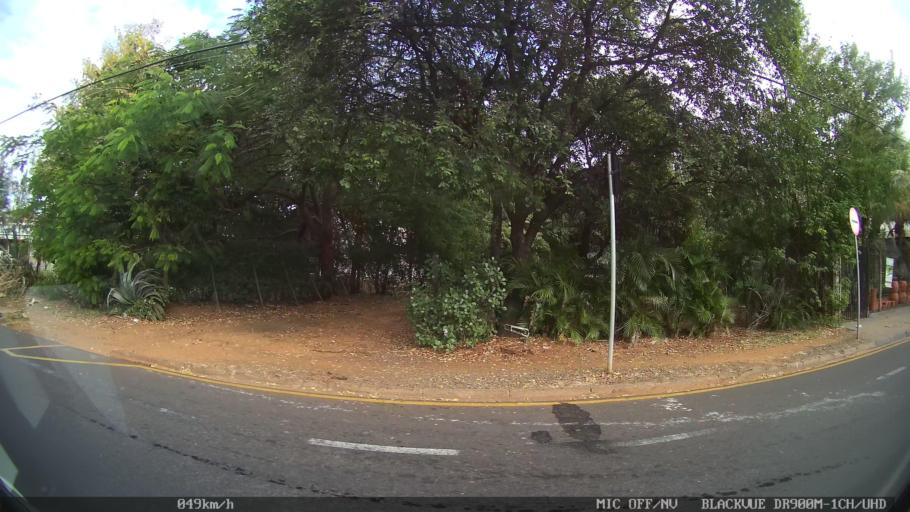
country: BR
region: Sao Paulo
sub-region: Sao Jose Do Rio Preto
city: Sao Jose do Rio Preto
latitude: -20.8366
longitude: -49.3712
